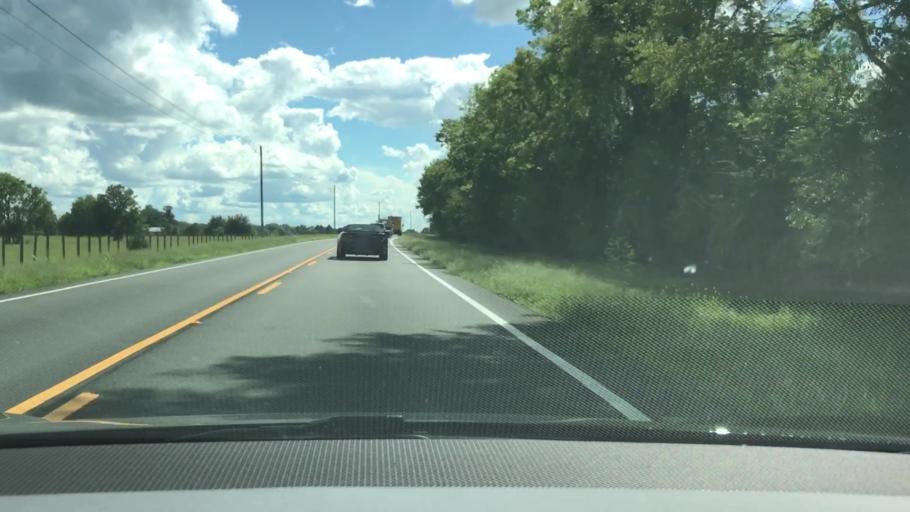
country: US
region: Alabama
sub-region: Montgomery County
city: Pike Road
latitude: 32.3143
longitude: -86.0974
